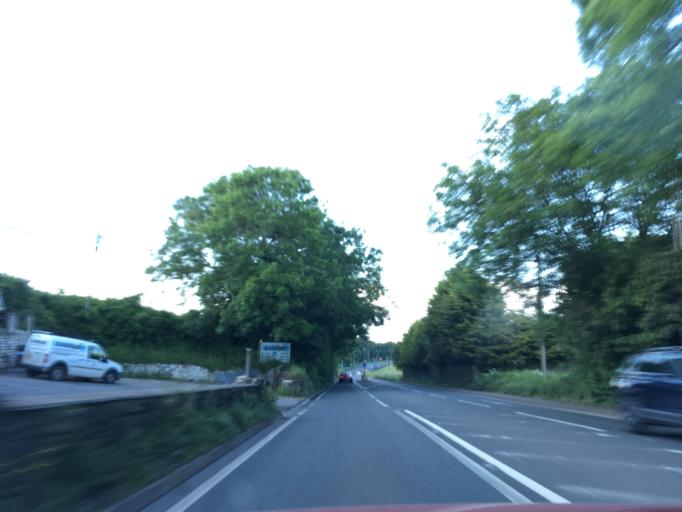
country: GB
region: England
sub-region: North Somerset
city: Winford
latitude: 51.4024
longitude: -2.6716
